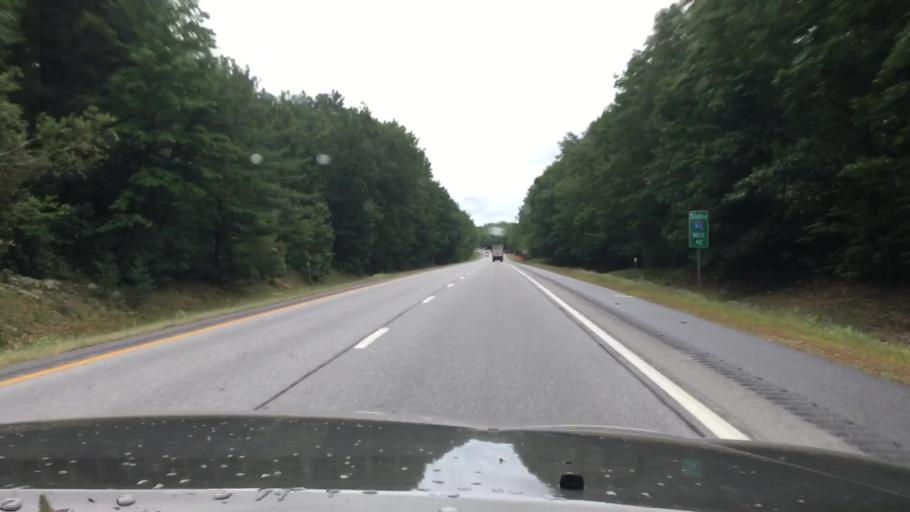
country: US
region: New Hampshire
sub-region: Merrimack County
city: East Concord
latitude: 43.2584
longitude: -71.5511
